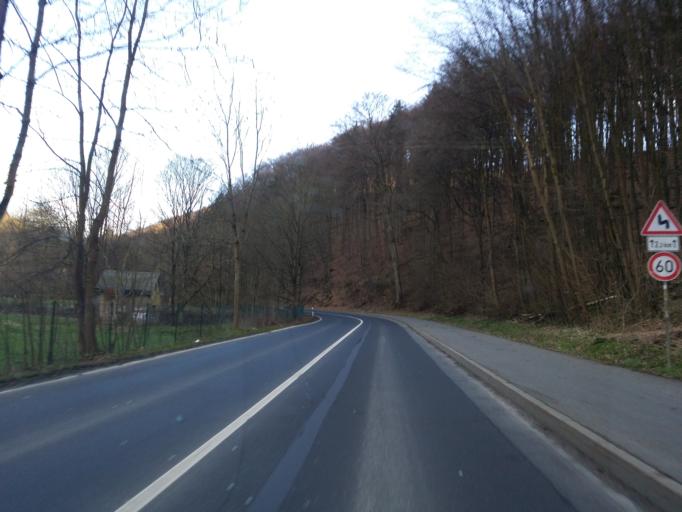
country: DE
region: Hesse
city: Eppstein
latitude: 50.1323
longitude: 8.4023
